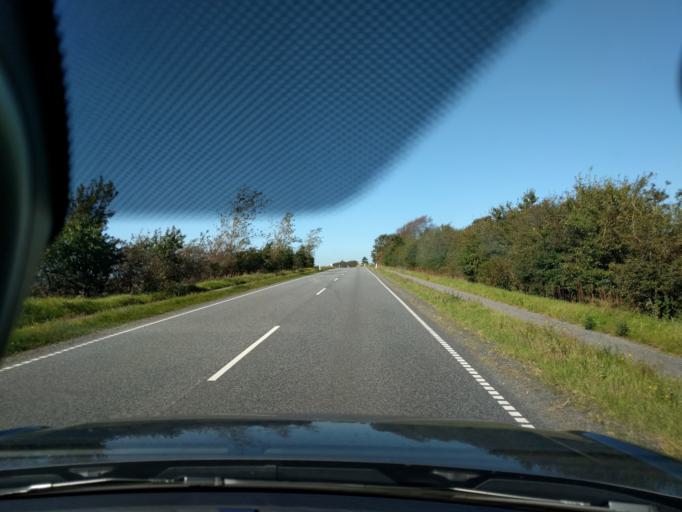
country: DK
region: North Denmark
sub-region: Vesthimmerland Kommune
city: Aars
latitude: 56.7372
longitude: 9.6004
